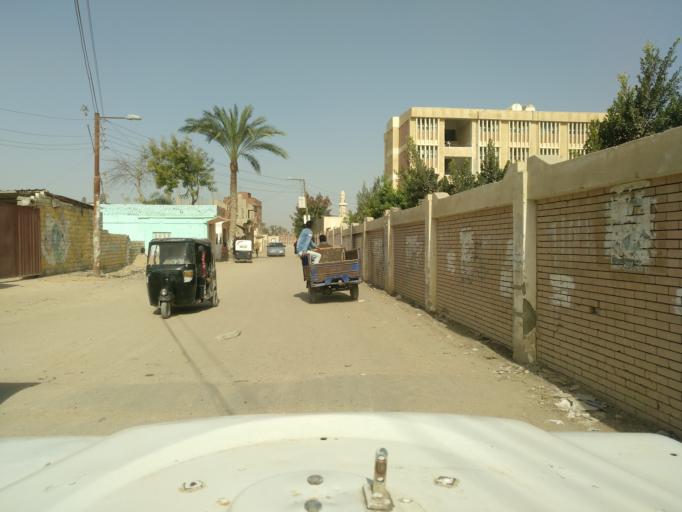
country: EG
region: Al Buhayrah
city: Beheira
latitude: 30.3778
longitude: 30.3470
